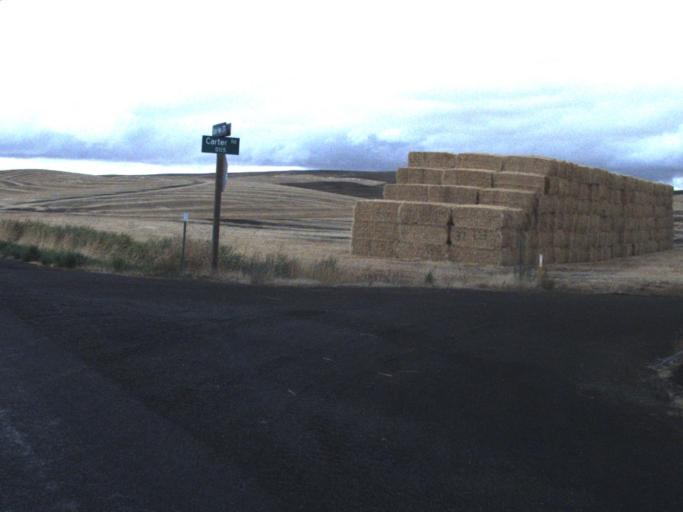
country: US
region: Washington
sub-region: Whitman County
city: Colfax
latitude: 47.1621
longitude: -117.2687
